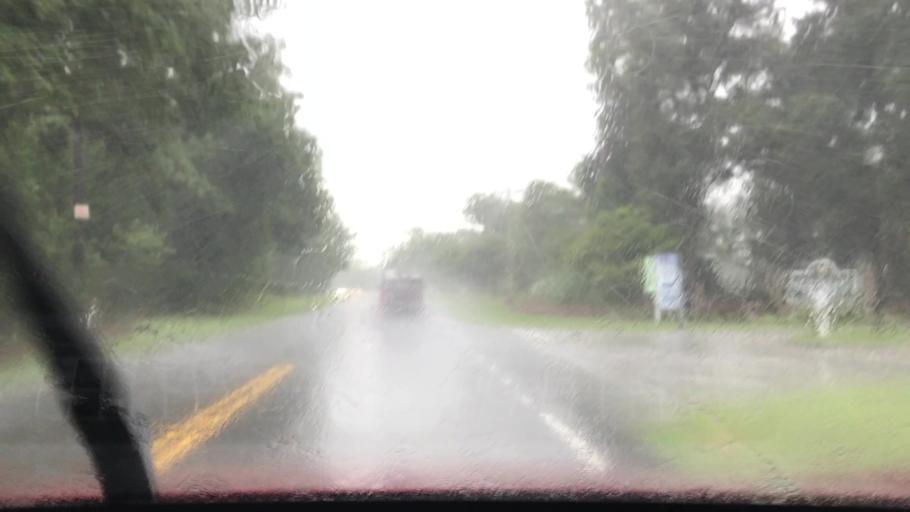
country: US
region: South Carolina
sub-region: Horry County
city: Red Hill
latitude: 33.9023
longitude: -78.8967
